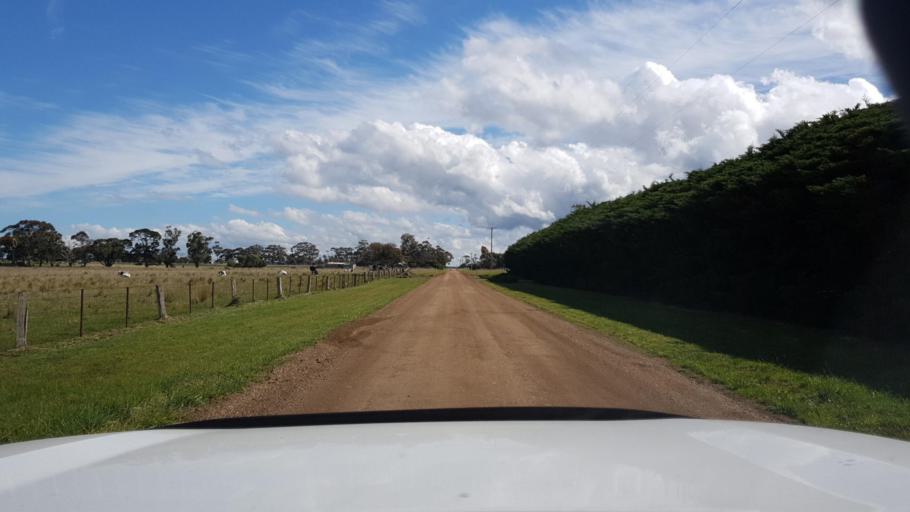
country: AU
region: Victoria
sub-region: Hume
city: Sunbury
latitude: -37.5839
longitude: 144.6513
